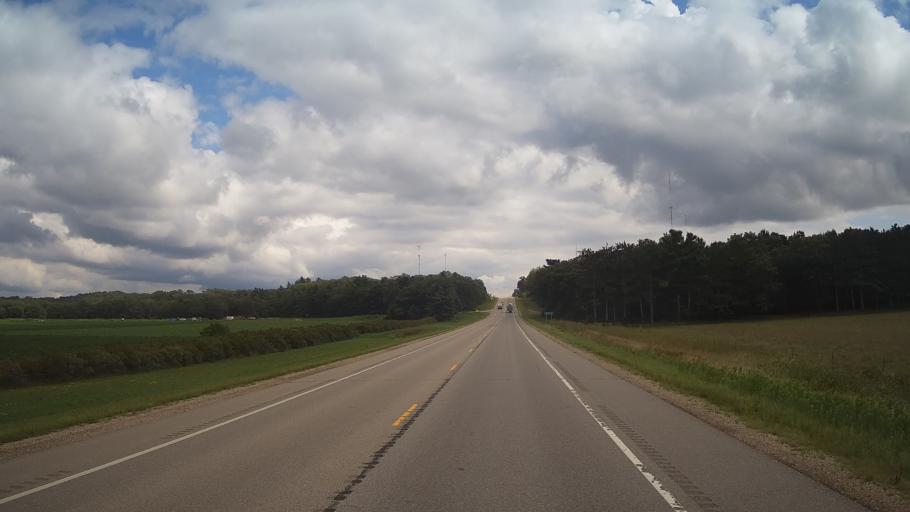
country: US
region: Wisconsin
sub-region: Marquette County
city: Westfield
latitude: 44.0219
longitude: -89.5791
